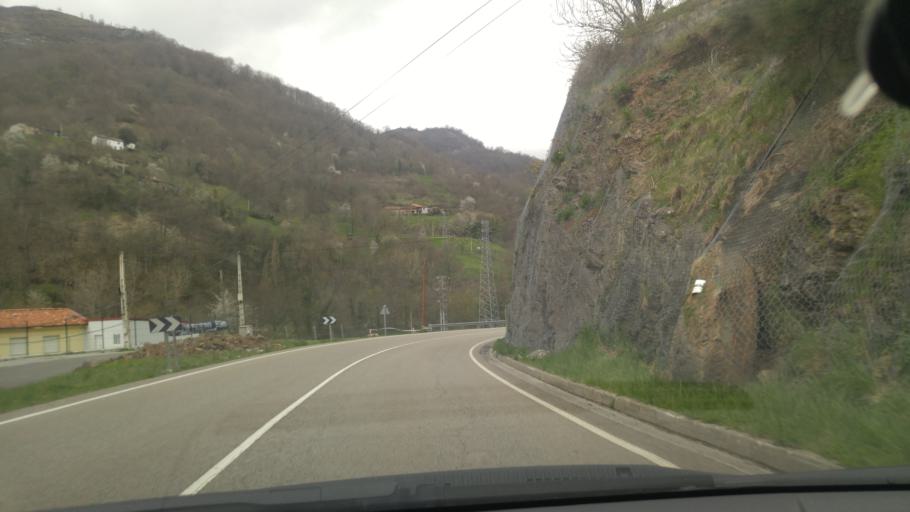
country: ES
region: Asturias
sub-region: Province of Asturias
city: Rio Aller
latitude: 43.1392
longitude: -5.5742
